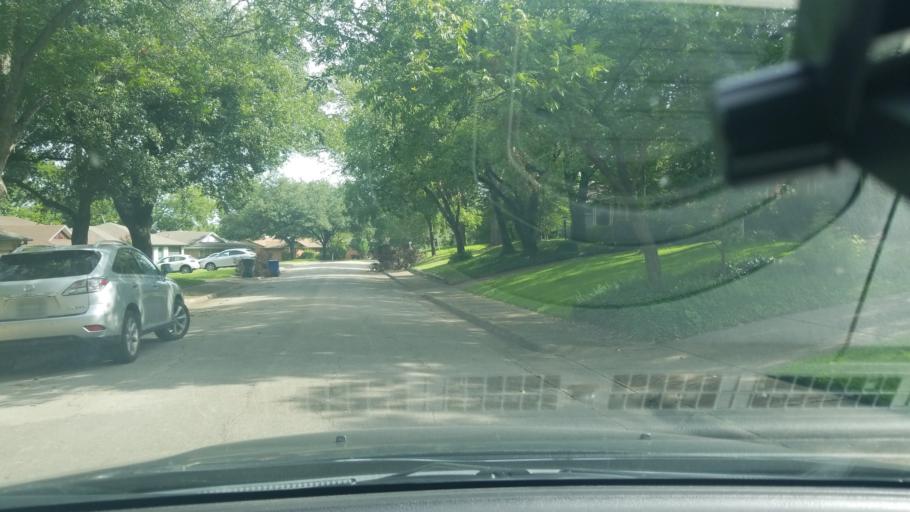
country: US
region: Texas
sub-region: Dallas County
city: Highland Park
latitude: 32.8093
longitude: -96.7027
